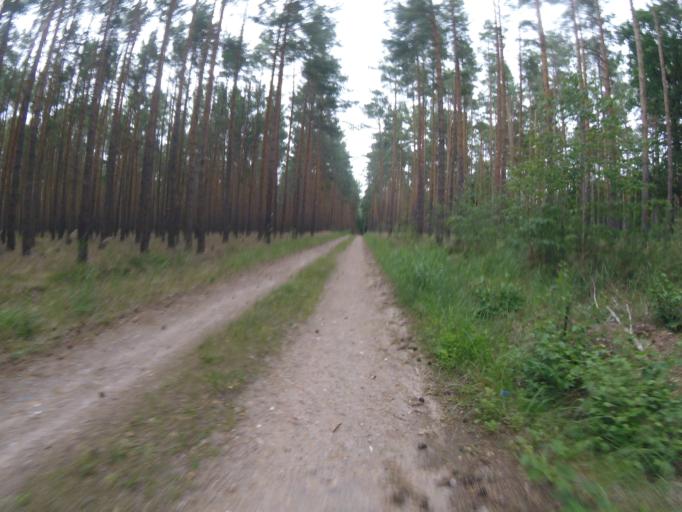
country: DE
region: Brandenburg
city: Gross Koris
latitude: 52.2027
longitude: 13.6759
